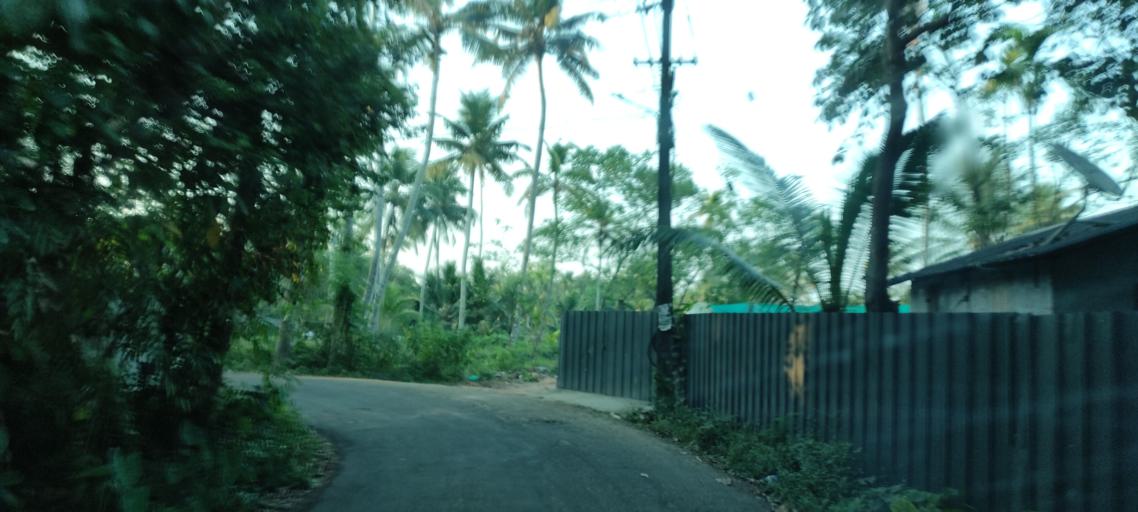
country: IN
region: Kerala
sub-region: Alappuzha
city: Kutiatodu
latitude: 9.7876
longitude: 76.3218
